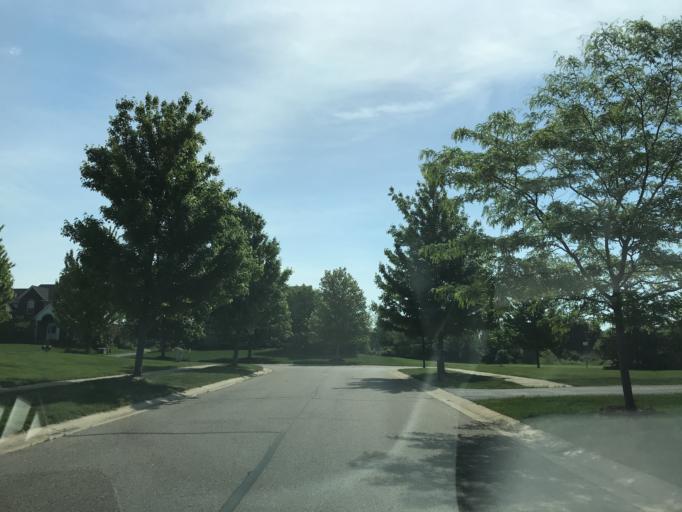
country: US
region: Michigan
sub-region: Oakland County
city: South Lyon
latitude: 42.4766
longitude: -83.6351
